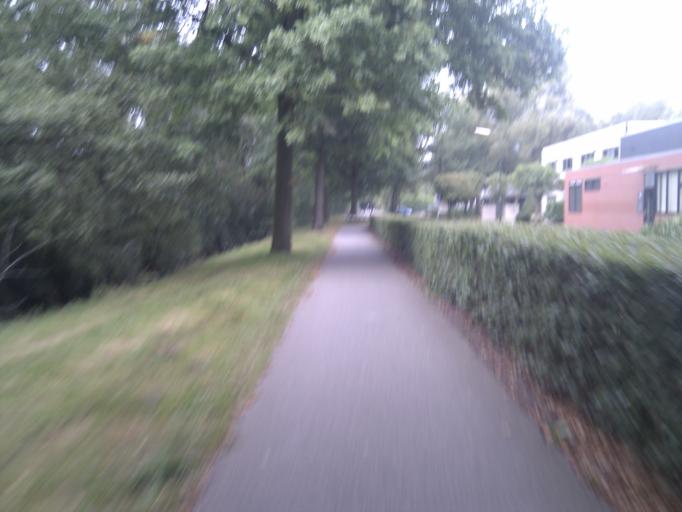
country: NL
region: Utrecht
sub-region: Gemeente De Bilt
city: De Bilt
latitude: 52.1090
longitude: 5.1695
